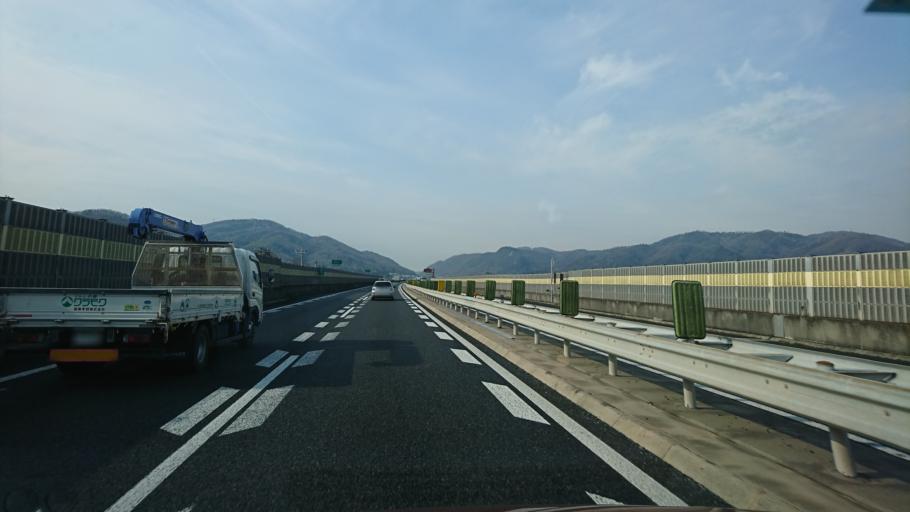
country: JP
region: Okayama
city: Okayama-shi
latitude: 34.7410
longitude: 134.0203
